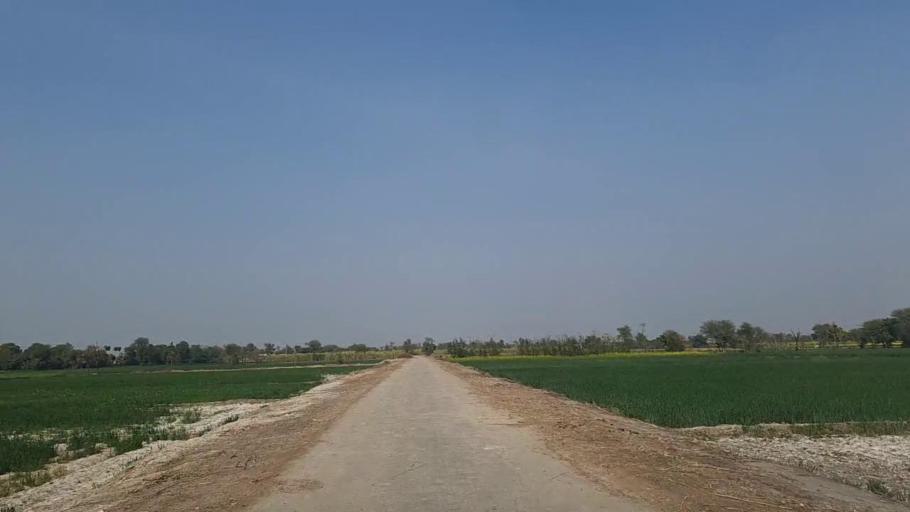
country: PK
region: Sindh
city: Daur
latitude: 26.4904
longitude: 68.4477
